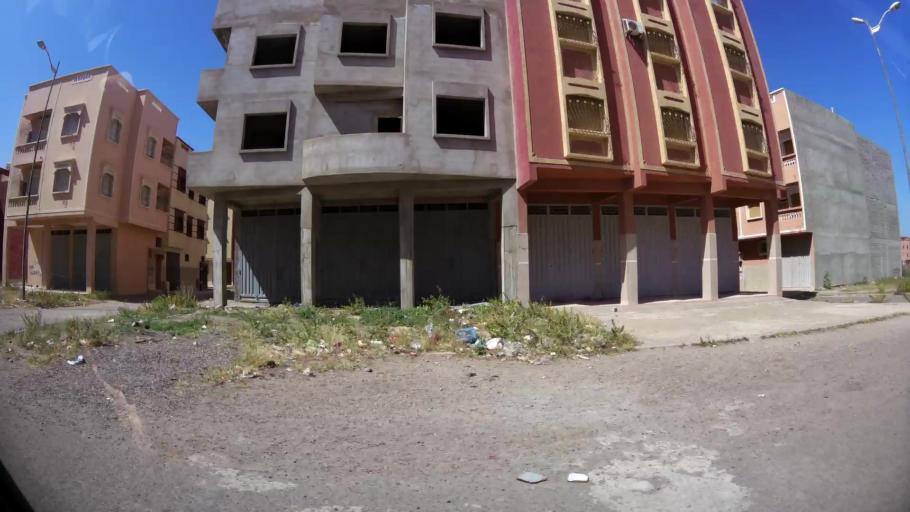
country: MA
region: Souss-Massa-Draa
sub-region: Inezgane-Ait Mellou
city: Inezgane
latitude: 30.3319
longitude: -9.5090
